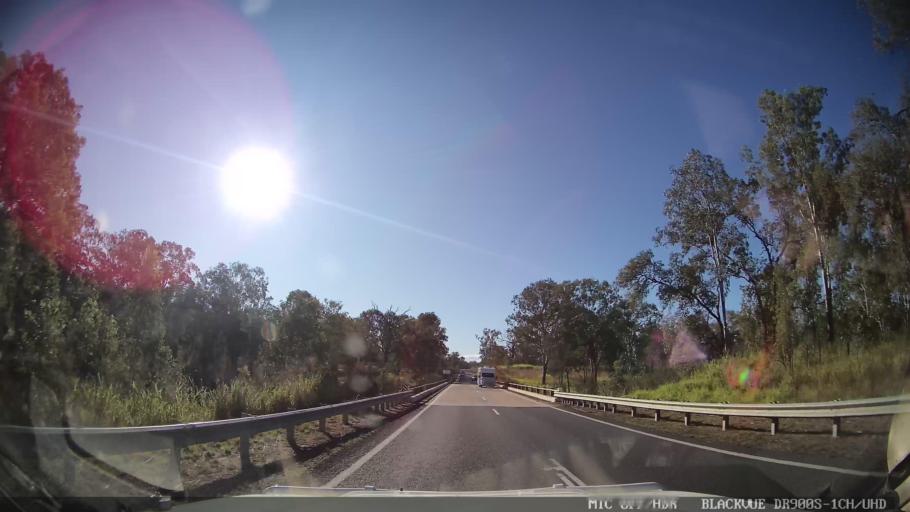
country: AU
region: Queensland
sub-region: Bundaberg
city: Sharon
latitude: -24.8287
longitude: 151.7081
